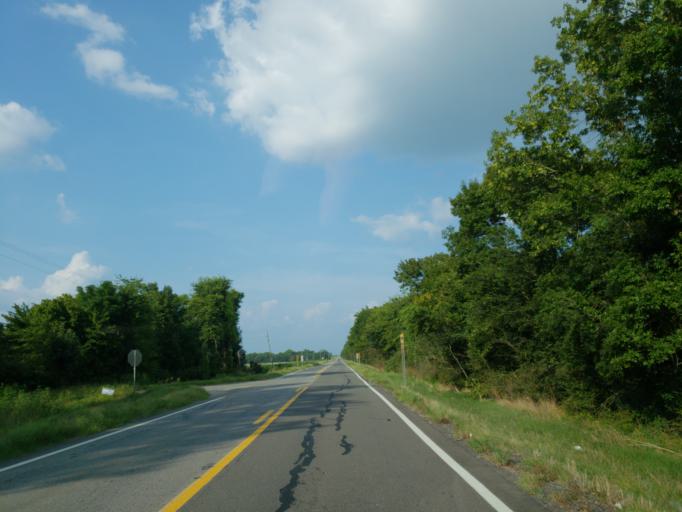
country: US
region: Alabama
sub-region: Greene County
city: Eutaw
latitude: 32.7944
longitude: -87.9692
